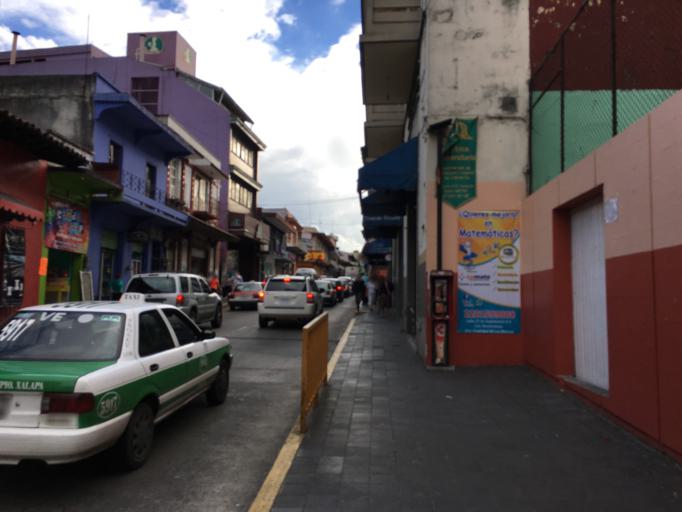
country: MX
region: Veracruz
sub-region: Xalapa
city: Xalapa de Enriquez
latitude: 19.5289
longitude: -96.9189
